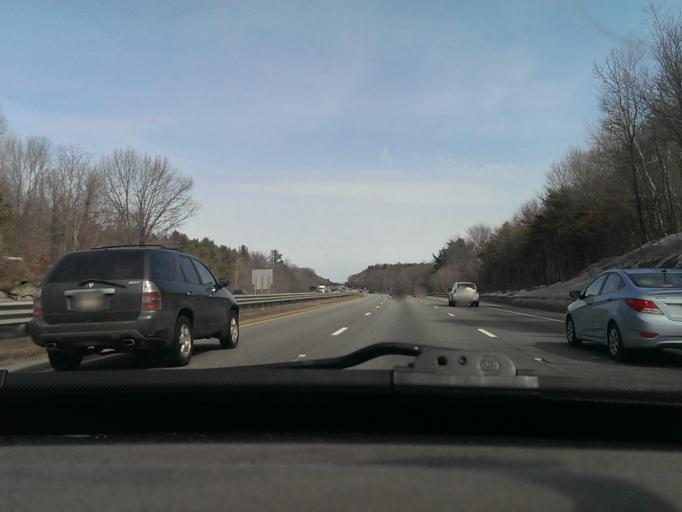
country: US
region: Massachusetts
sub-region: Worcester County
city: Charlton
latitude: 42.1634
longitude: -71.9459
